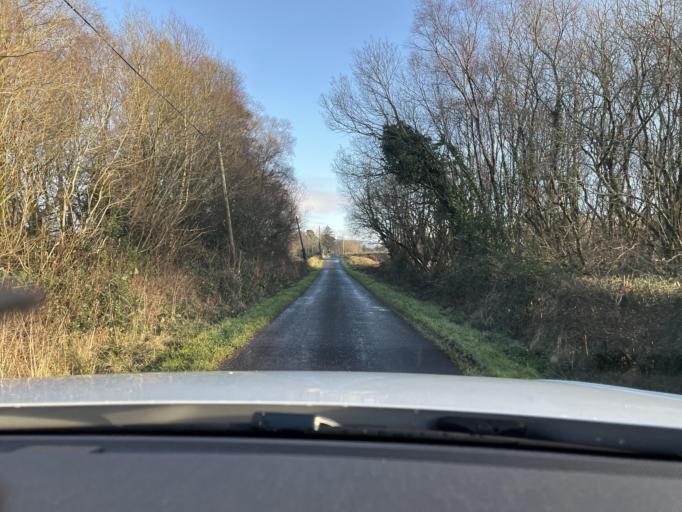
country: IE
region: Connaught
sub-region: County Leitrim
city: Manorhamilton
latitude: 54.2154
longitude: -7.9711
